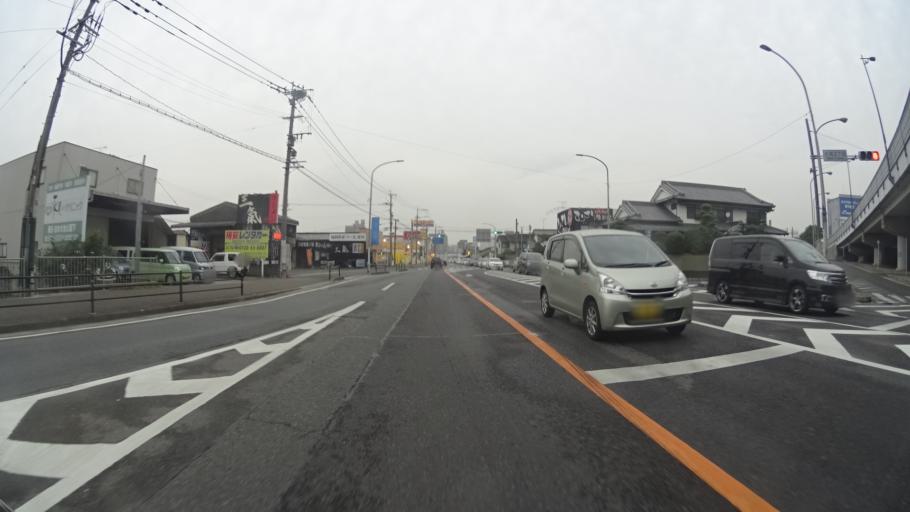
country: JP
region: Fukuoka
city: Onojo
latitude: 33.5247
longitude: 130.4952
